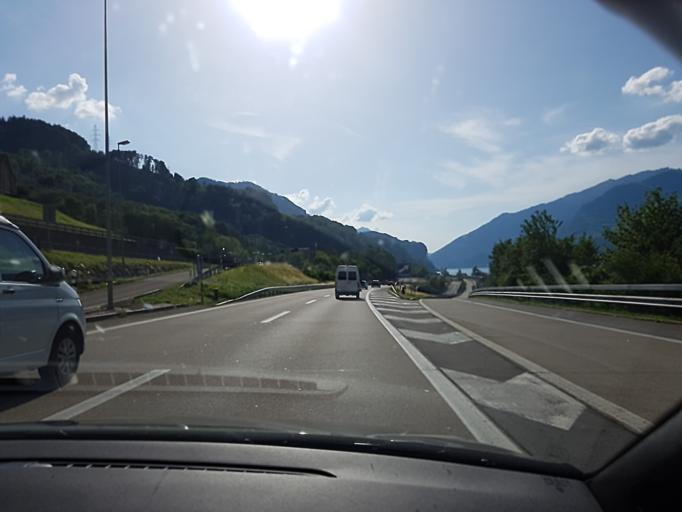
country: CH
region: Saint Gallen
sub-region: Wahlkreis Sarganserland
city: Quarten
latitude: 47.1151
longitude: 9.1998
